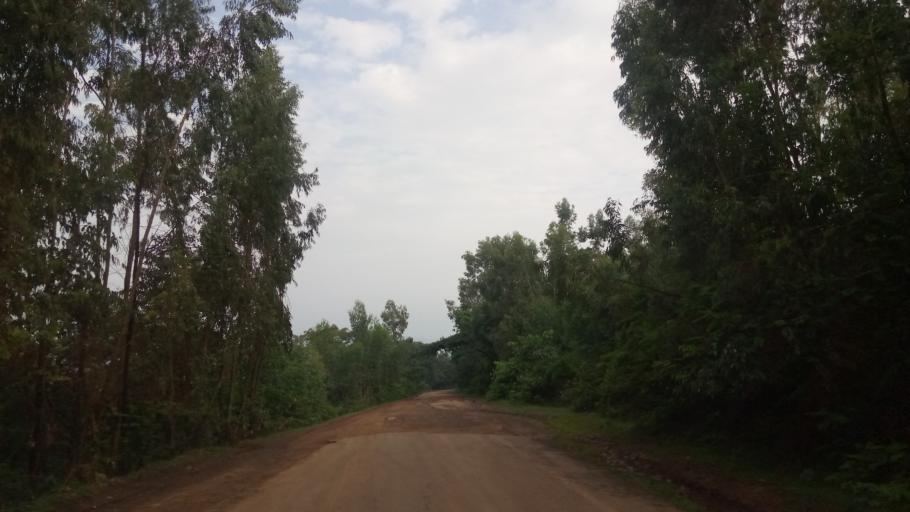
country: ET
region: Oromiya
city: Agaro
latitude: 7.7979
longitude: 36.7170
